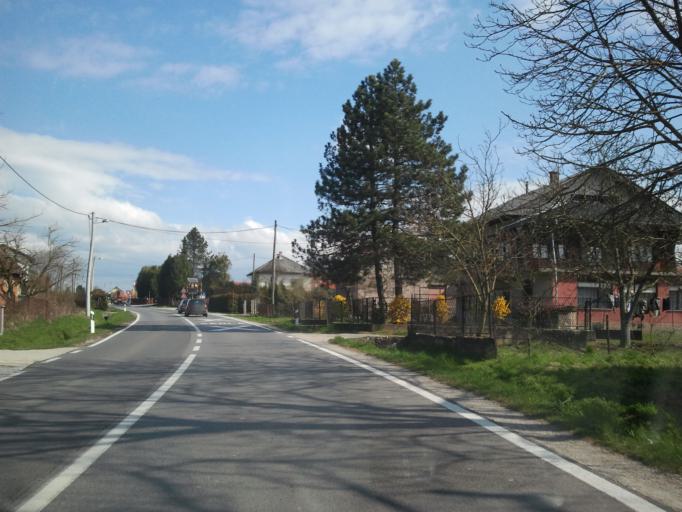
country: HR
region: Karlovacka
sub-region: Grad Karlovac
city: Karlovac
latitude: 45.5699
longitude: 15.5926
